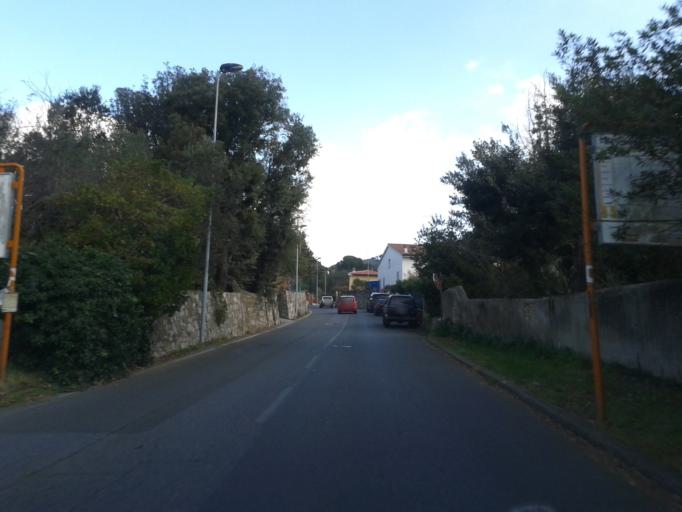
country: IT
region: Tuscany
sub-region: Provincia di Livorno
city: Quercianella
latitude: 43.4987
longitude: 10.3448
